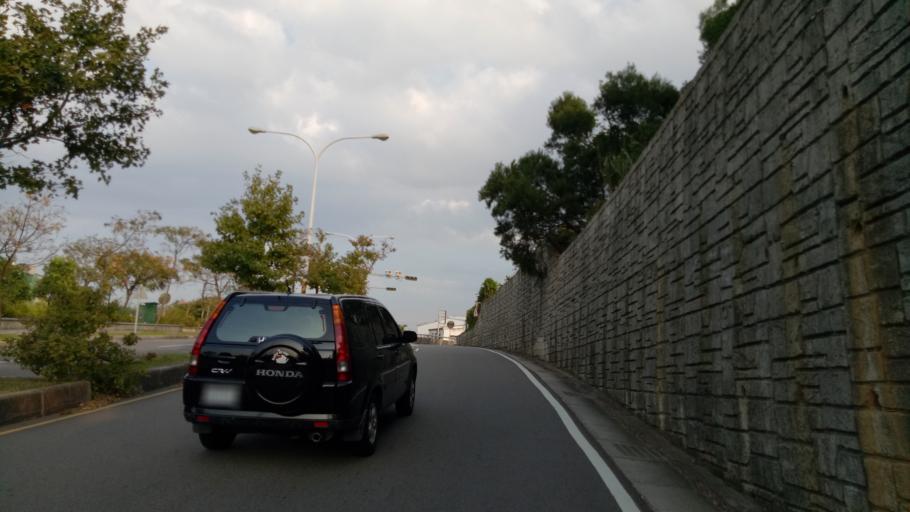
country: TW
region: Taiwan
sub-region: Hsinchu
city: Hsinchu
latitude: 24.7691
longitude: 121.0035
